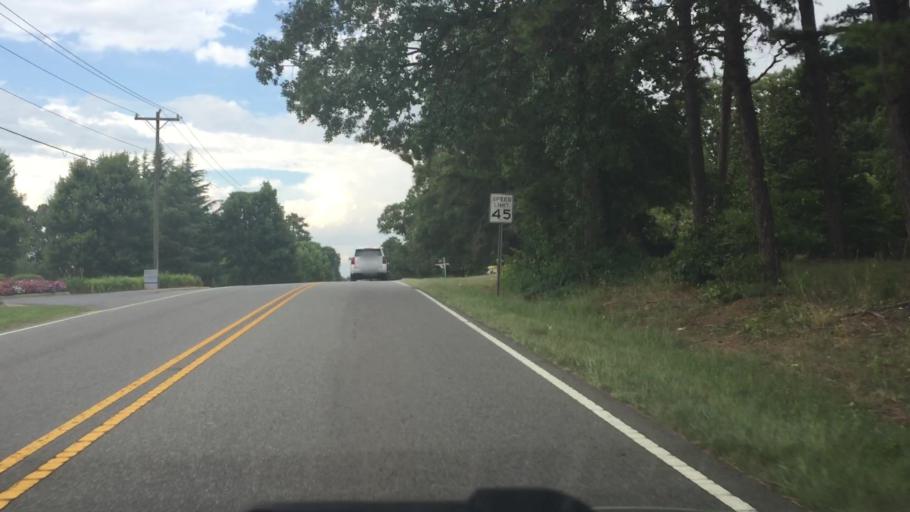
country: US
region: North Carolina
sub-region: Cabarrus County
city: Harrisburg
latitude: 35.4154
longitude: -80.7095
